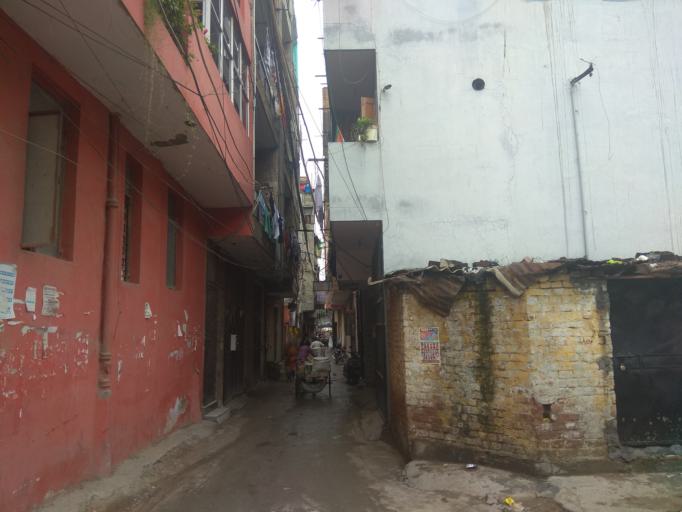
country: IN
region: NCT
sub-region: New Delhi
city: New Delhi
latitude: 28.5734
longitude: 77.2553
